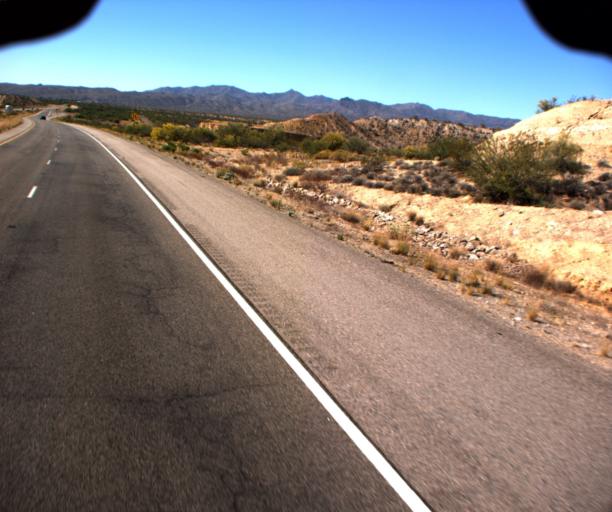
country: US
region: Arizona
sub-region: Yavapai County
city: Bagdad
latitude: 34.7476
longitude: -113.6166
